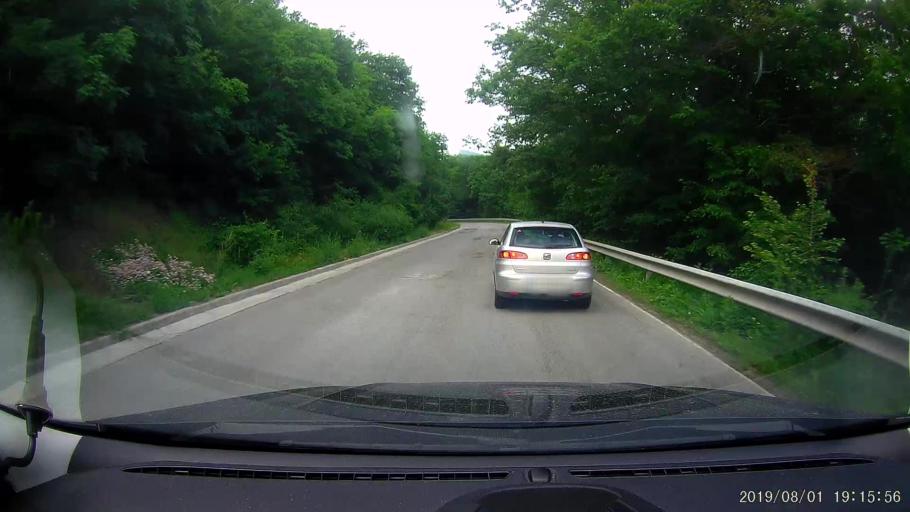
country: BG
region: Shumen
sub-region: Obshtina Smyadovo
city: Smyadovo
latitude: 42.9293
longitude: 26.9454
